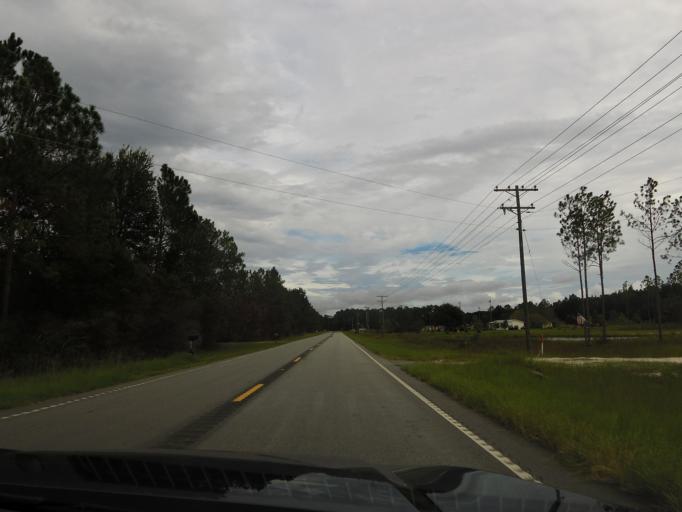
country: US
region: Florida
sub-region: Nassau County
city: Hilliard
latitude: 30.5214
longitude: -82.0567
